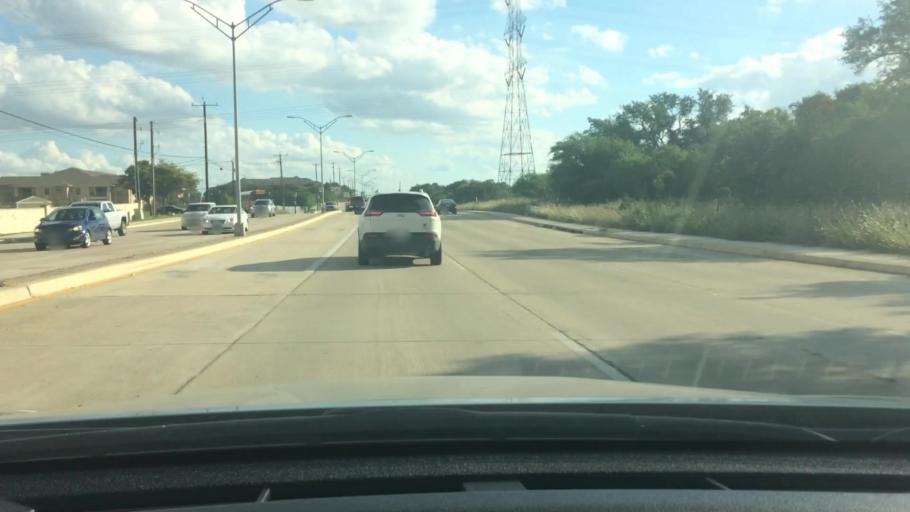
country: US
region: Texas
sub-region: Bexar County
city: Hollywood Park
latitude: 29.6370
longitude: -98.4242
